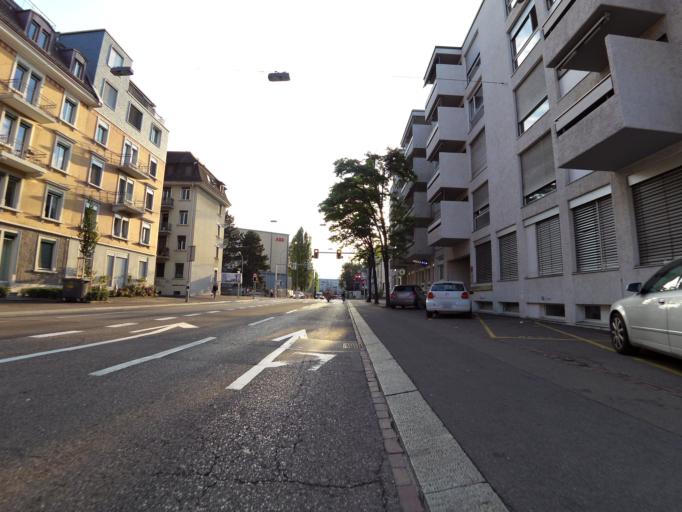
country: CH
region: Zurich
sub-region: Bezirk Zuerich
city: Zuerich (Kreis 11) / Oerlikon
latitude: 47.4140
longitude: 8.5450
